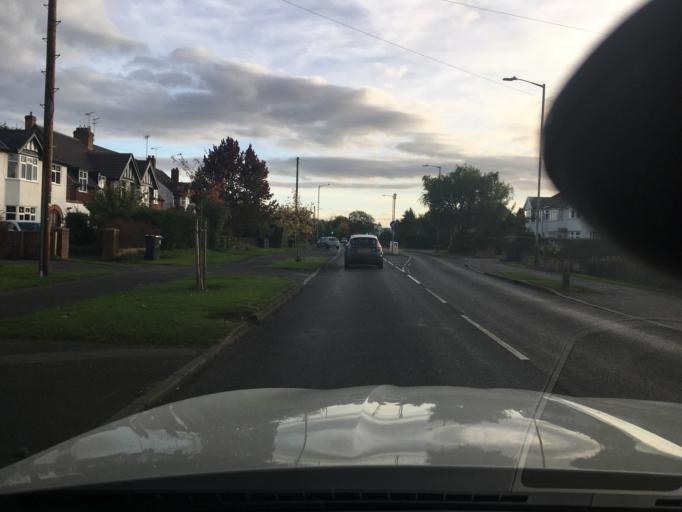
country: GB
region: England
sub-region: Warwickshire
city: Warwick
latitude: 52.2735
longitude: -1.5963
